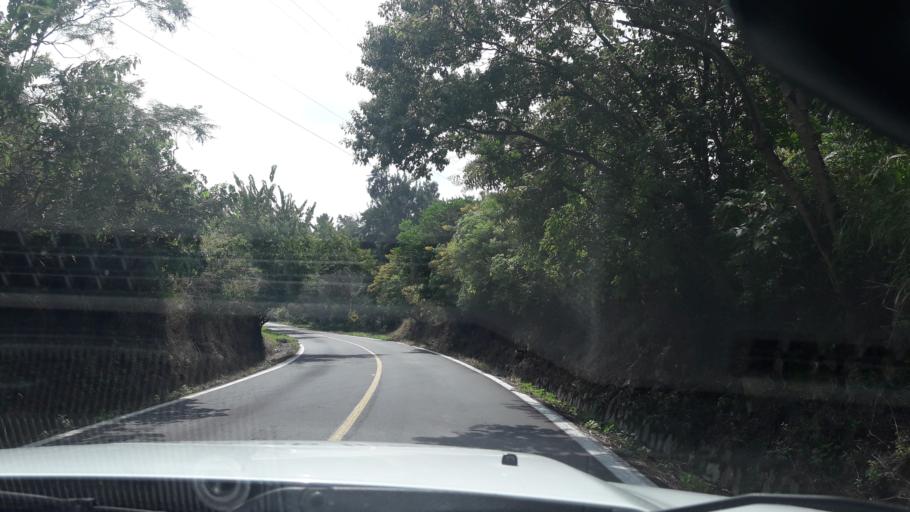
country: MX
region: Colima
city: Suchitlan
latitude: 19.3899
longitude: -103.7079
